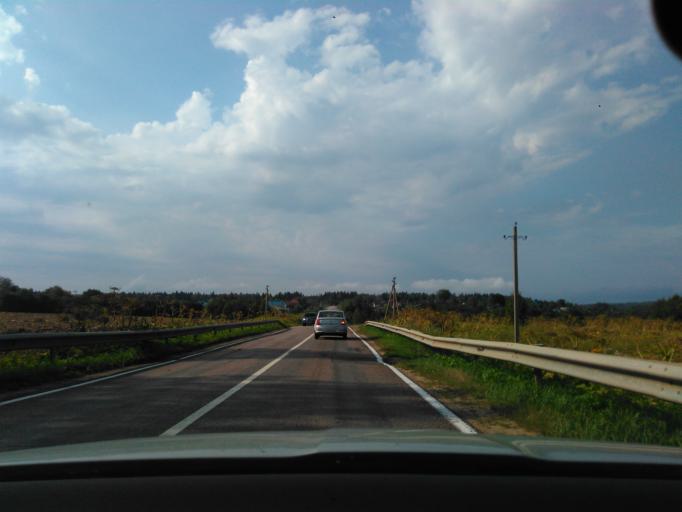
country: RU
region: Moskovskaya
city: Klin
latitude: 56.1602
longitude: 36.7446
